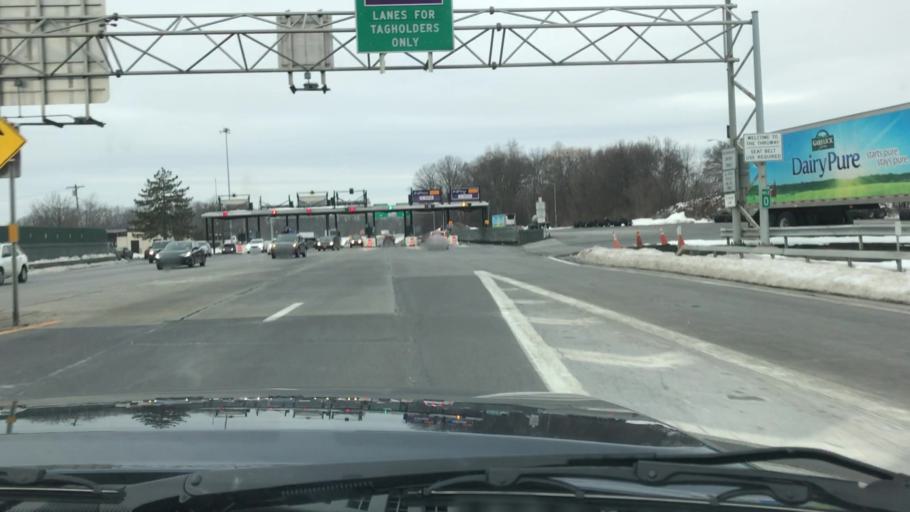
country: US
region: New York
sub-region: Albany County
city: Albany
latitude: 42.6331
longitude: -73.7768
